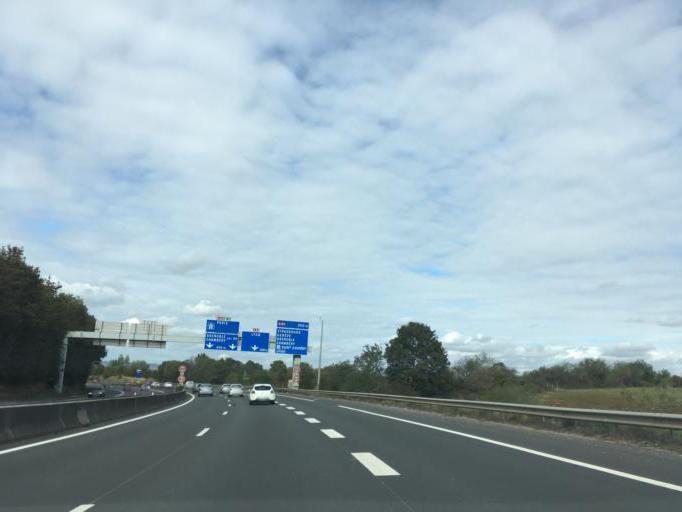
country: FR
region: Rhone-Alpes
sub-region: Departement du Rhone
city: Saint-Priest
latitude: 45.6980
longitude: 4.9723
